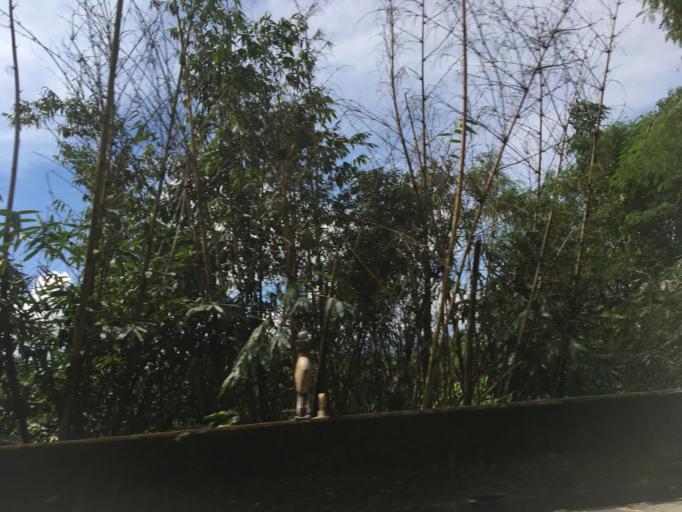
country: TW
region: Taiwan
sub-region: Yilan
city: Yilan
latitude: 24.6664
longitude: 121.5955
